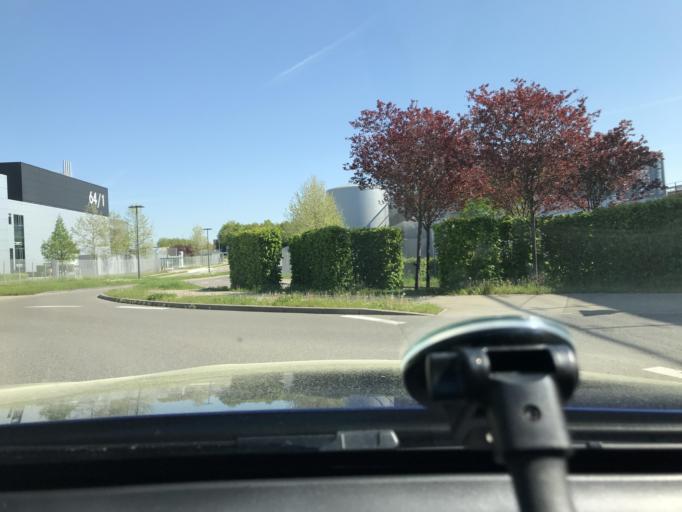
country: DE
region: Baden-Wuerttemberg
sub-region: Regierungsbezirk Stuttgart
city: Magstadt
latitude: 48.7017
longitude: 8.9814
